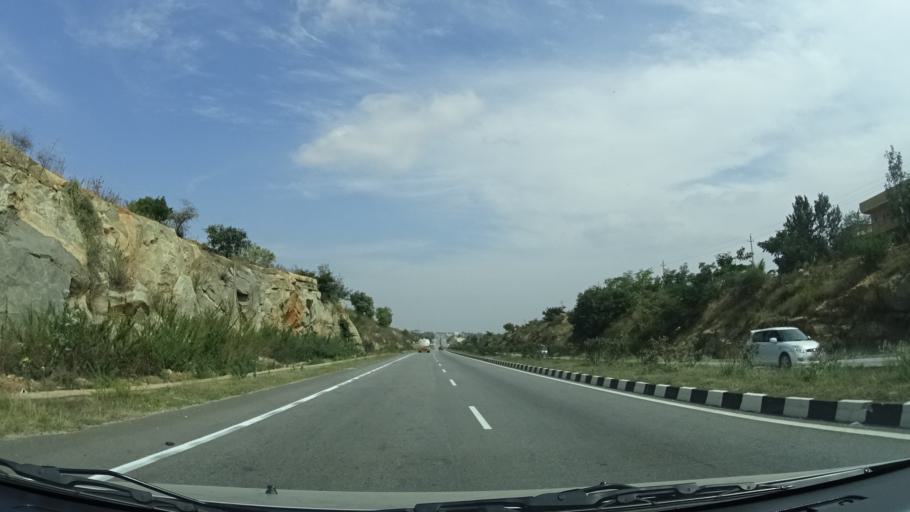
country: IN
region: Karnataka
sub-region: Chikkaballapur
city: Gudibanda
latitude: 13.5637
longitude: 77.7790
